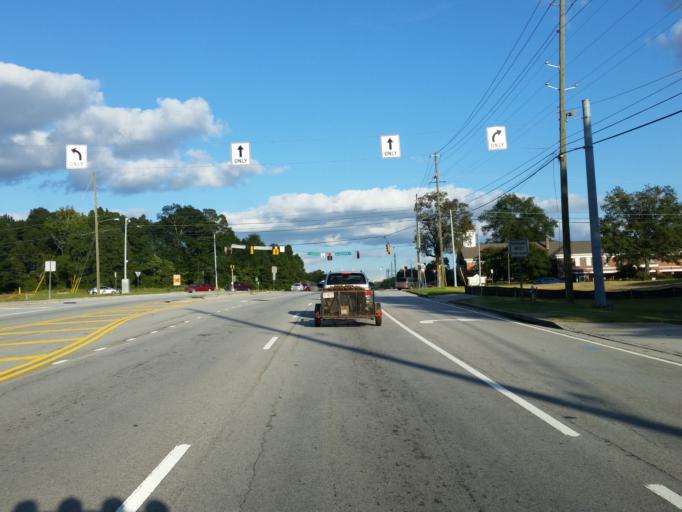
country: US
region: Georgia
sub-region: Cobb County
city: Powder Springs
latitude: 33.9025
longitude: -84.6739
